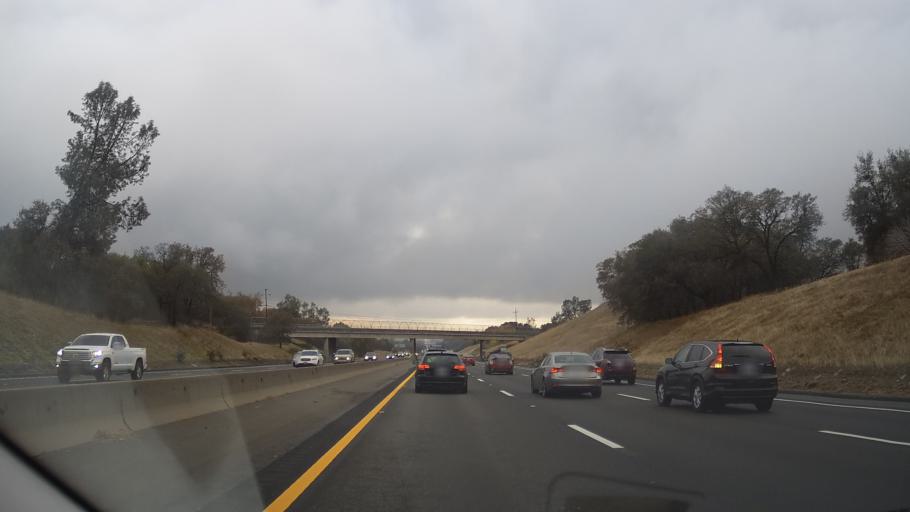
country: US
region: California
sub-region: Placer County
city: Newcastle
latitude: 38.8558
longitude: -121.1423
